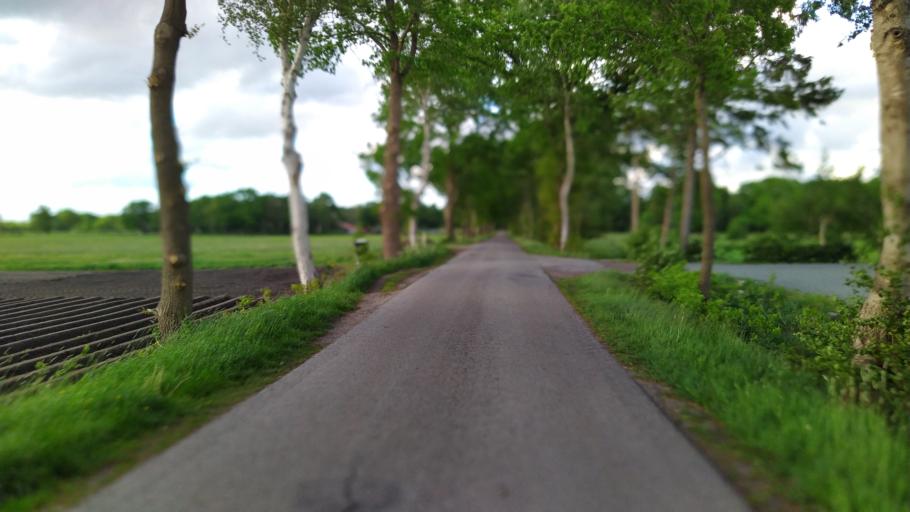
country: DE
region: Lower Saxony
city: Bargstedt
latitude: 53.4804
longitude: 9.4243
